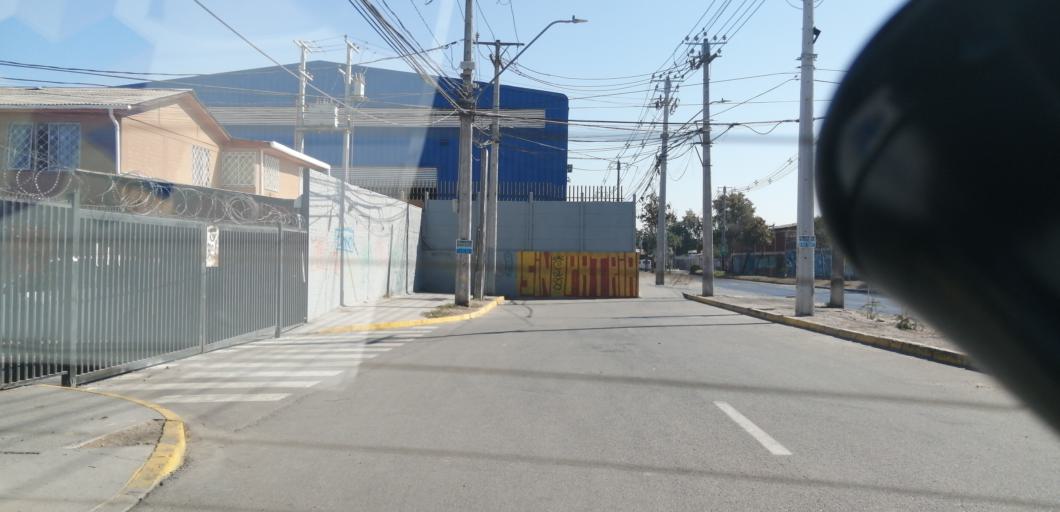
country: CL
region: Santiago Metropolitan
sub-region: Provincia de Santiago
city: Lo Prado
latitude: -33.4447
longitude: -70.7686
